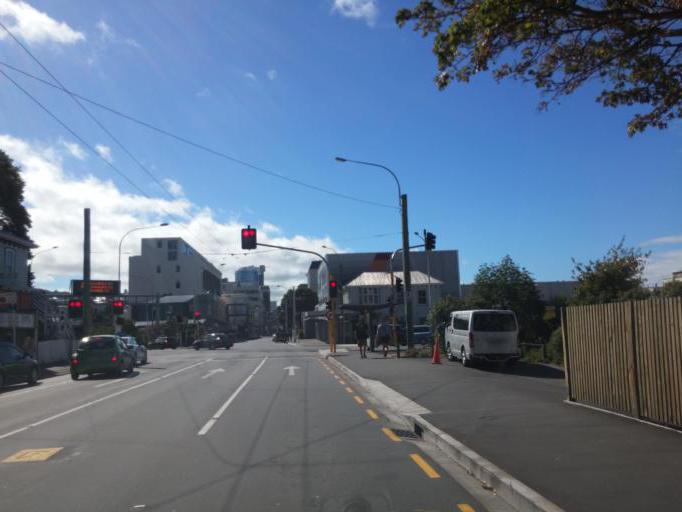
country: NZ
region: Wellington
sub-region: Wellington City
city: Wellington
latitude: -41.2959
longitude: 174.7710
